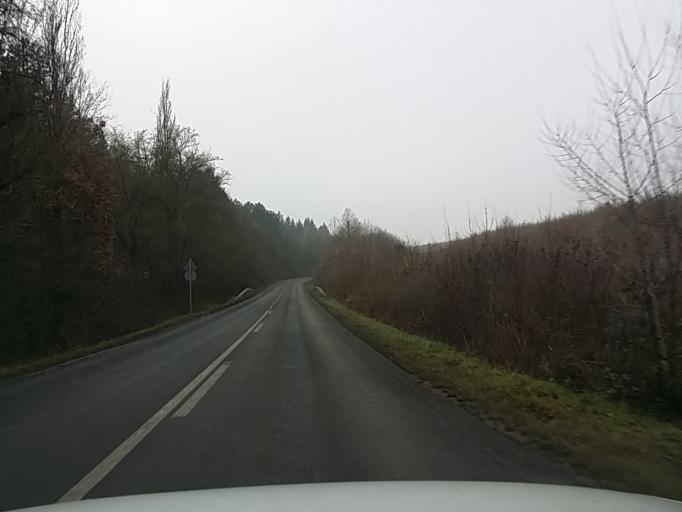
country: HU
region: Pest
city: Budakeszi
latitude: 47.5275
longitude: 18.8806
